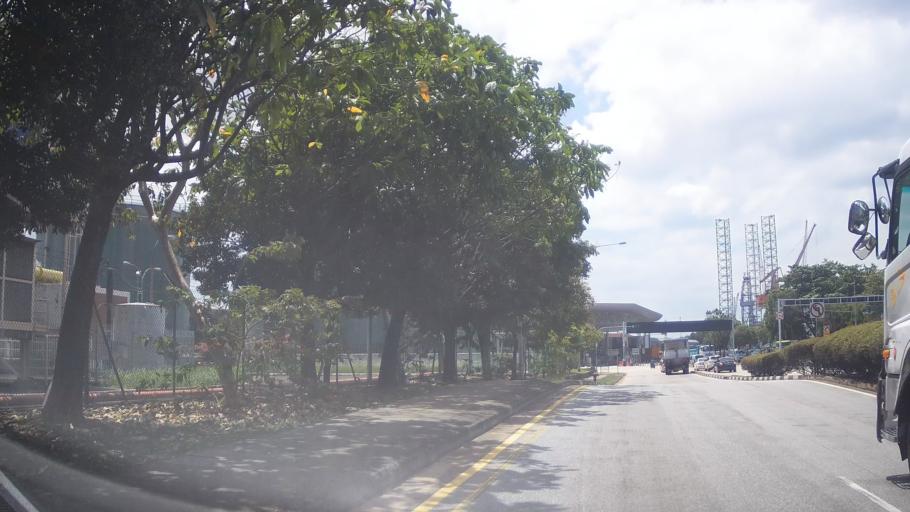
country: SG
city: Singapore
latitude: 1.3115
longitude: 103.7103
